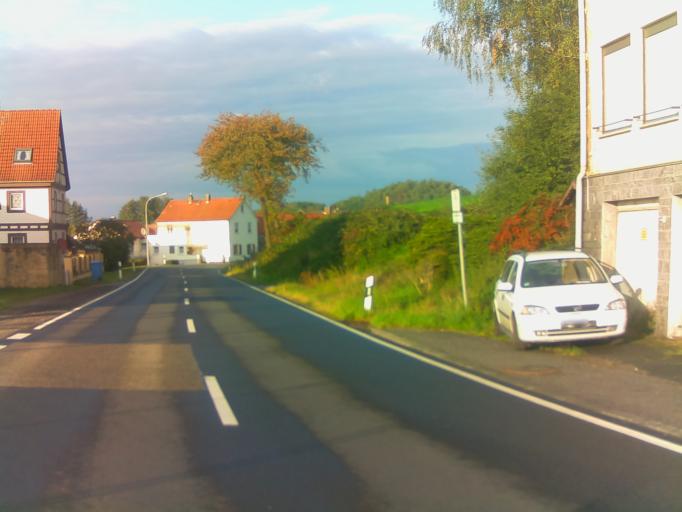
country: DE
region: Hesse
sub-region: Regierungsbezirk Darmstadt
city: Lindenfels
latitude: 49.6877
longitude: 8.8112
